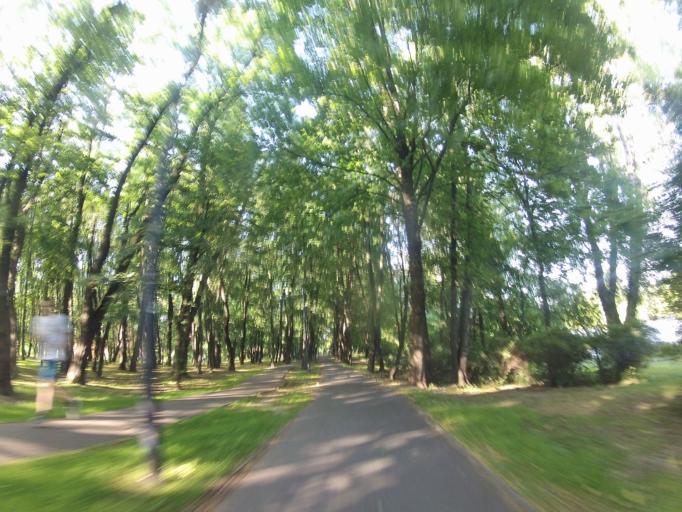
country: PL
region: Lesser Poland Voivodeship
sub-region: Krakow
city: Krakow
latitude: 50.0592
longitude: 19.9829
